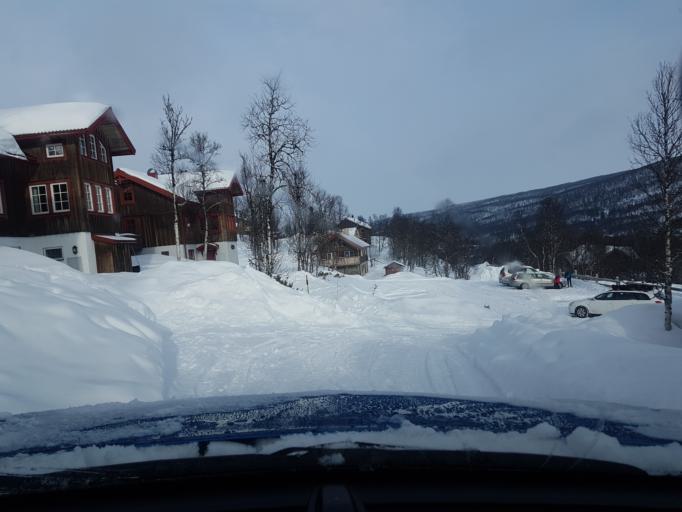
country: NO
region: Sor-Trondelag
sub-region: Tydal
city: Aas
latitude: 62.6912
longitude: 12.3992
